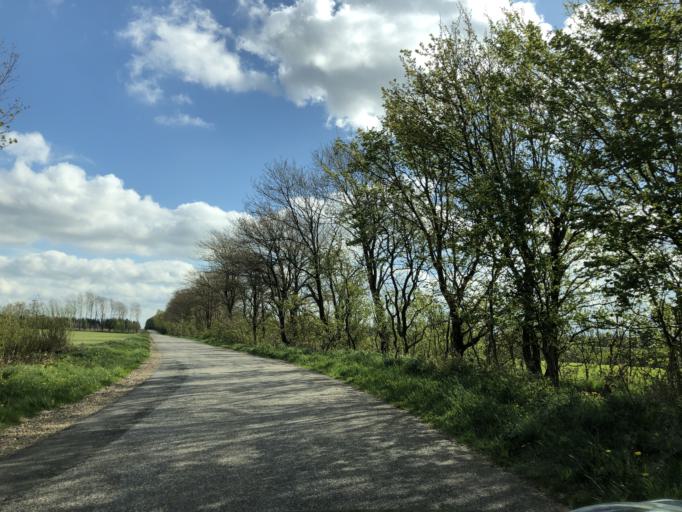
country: DK
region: Central Jutland
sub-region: Herning Kommune
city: Avlum
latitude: 56.2943
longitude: 8.6993
